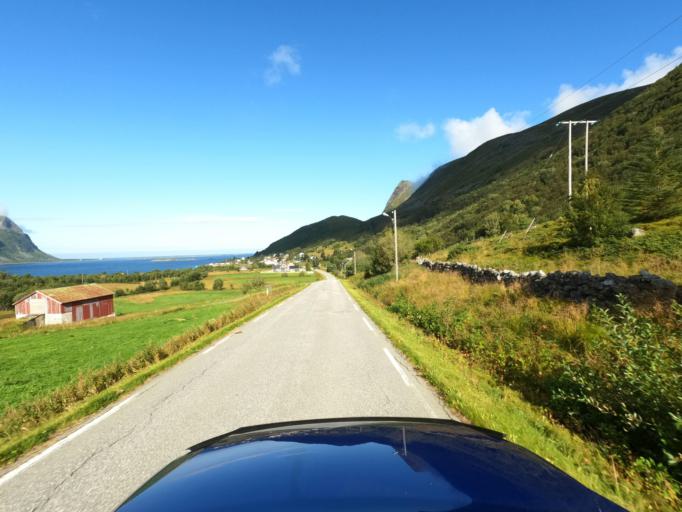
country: NO
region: Nordland
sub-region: Vagan
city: Kabelvag
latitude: 68.2958
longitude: 14.3242
